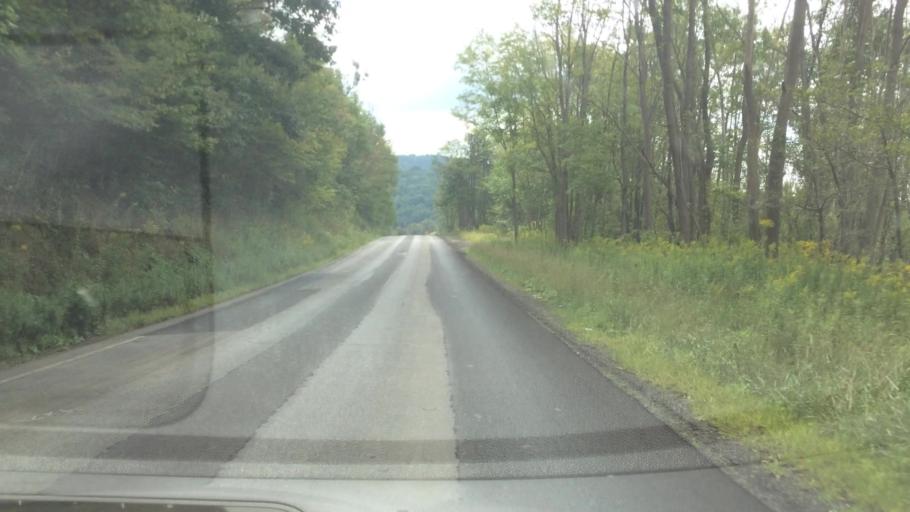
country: US
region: Pennsylvania
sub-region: McKean County
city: Bradford
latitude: 41.9177
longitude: -78.6436
